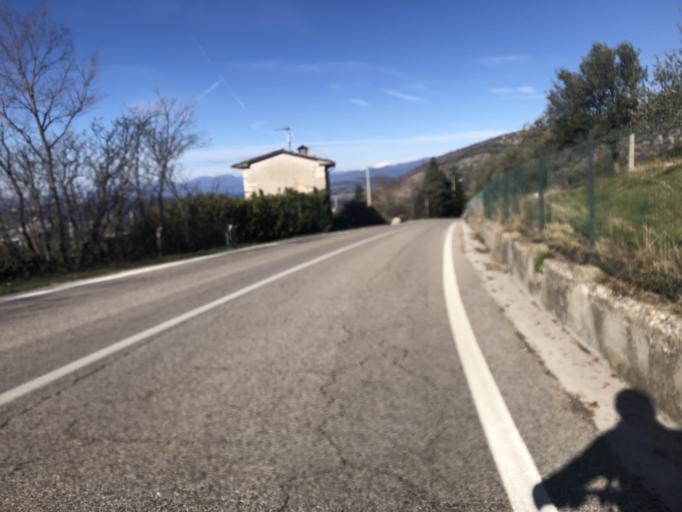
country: IT
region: Veneto
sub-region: Provincia di Verona
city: Dolce
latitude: 45.5629
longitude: 10.8511
